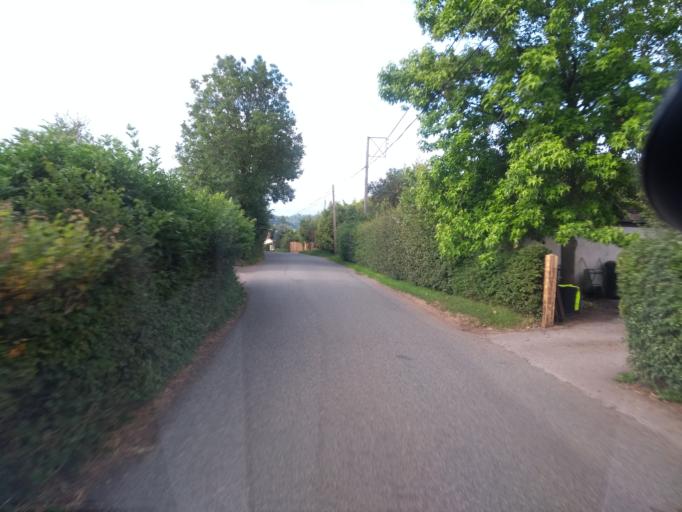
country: GB
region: England
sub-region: Somerset
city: Creech Saint Michael
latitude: 51.0130
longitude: -2.9774
